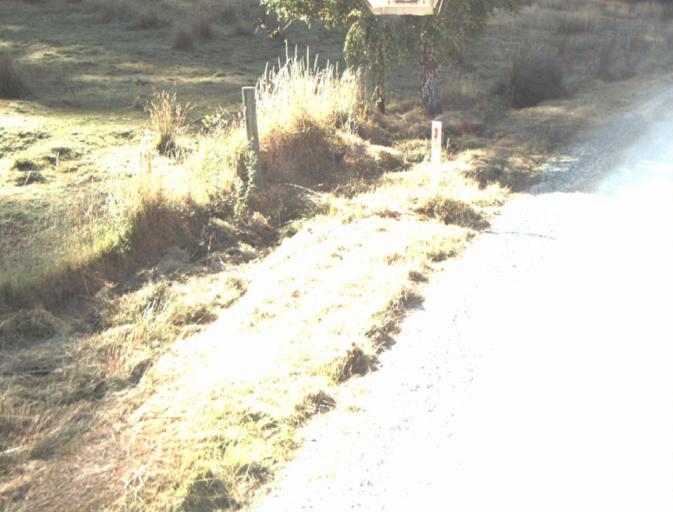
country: AU
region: Tasmania
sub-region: Launceston
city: Mayfield
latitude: -41.2875
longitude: 147.1972
